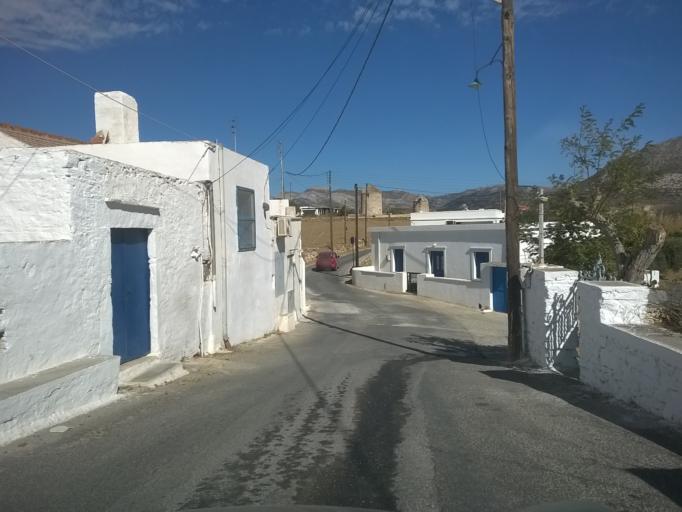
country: GR
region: South Aegean
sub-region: Nomos Kykladon
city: Filotion
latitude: 37.0404
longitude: 25.4350
